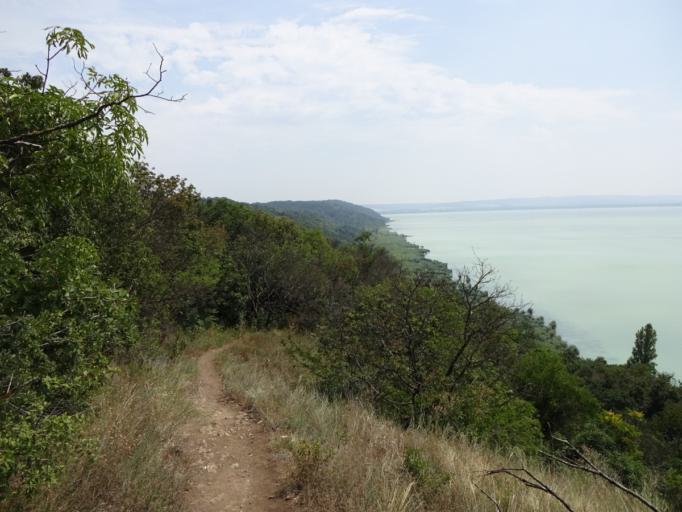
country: HU
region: Veszprem
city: Tihany
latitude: 46.9032
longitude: 17.8535
